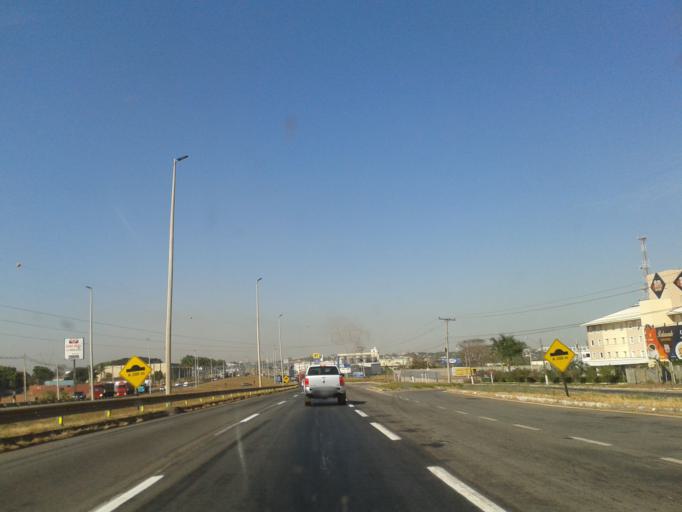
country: BR
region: Goias
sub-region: Aparecida De Goiania
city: Aparecida de Goiania
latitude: -16.7991
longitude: -49.2387
